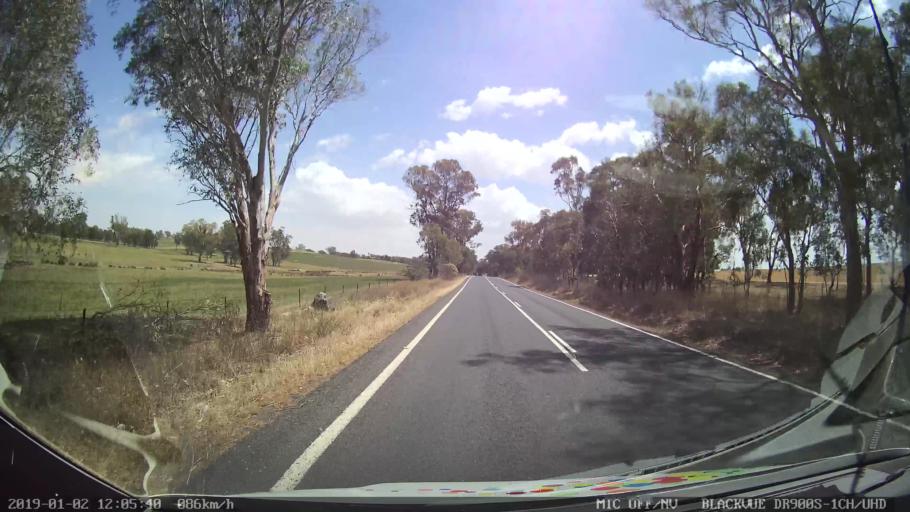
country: AU
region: New South Wales
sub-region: Young
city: Young
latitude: -34.5118
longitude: 148.3002
